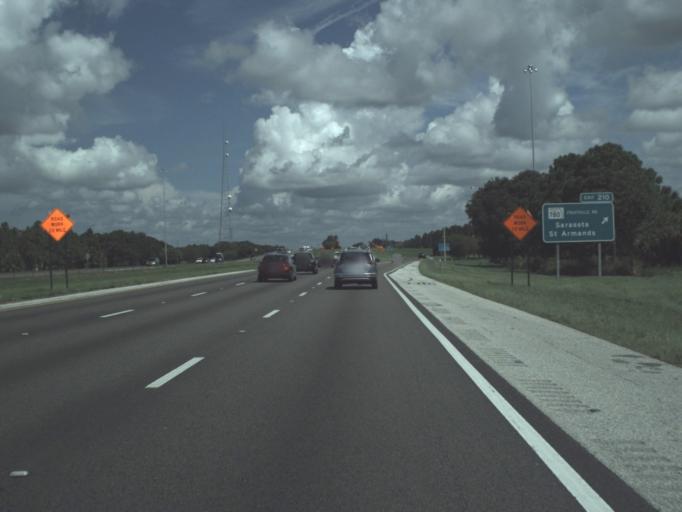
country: US
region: Florida
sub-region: Sarasota County
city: Fruitville
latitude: 27.3312
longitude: -82.4471
